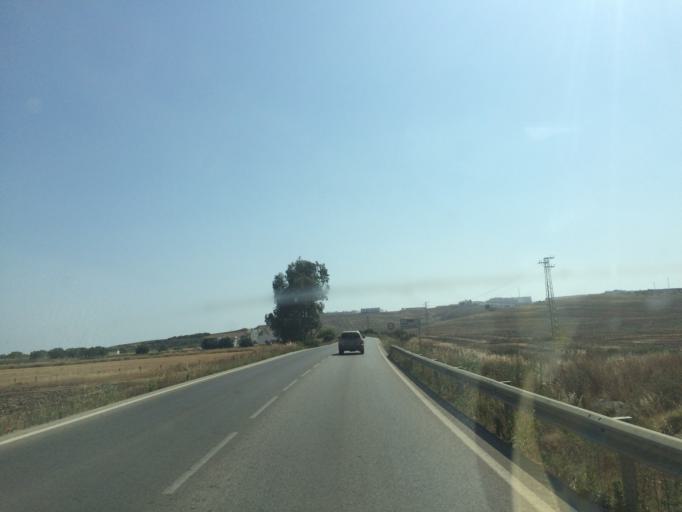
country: ES
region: Andalusia
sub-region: Provincia de Cadiz
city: Conil de la Frontera
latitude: 36.2879
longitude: -6.0668
